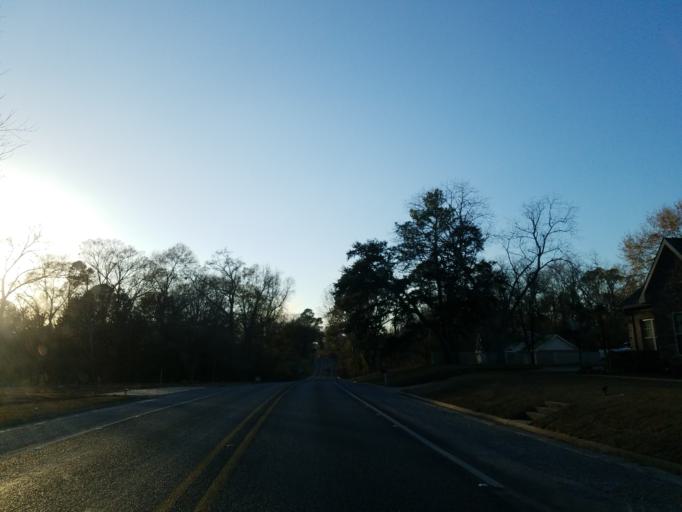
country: US
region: Mississippi
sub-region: Clarke County
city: Stonewall
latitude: 32.1758
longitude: -88.8214
